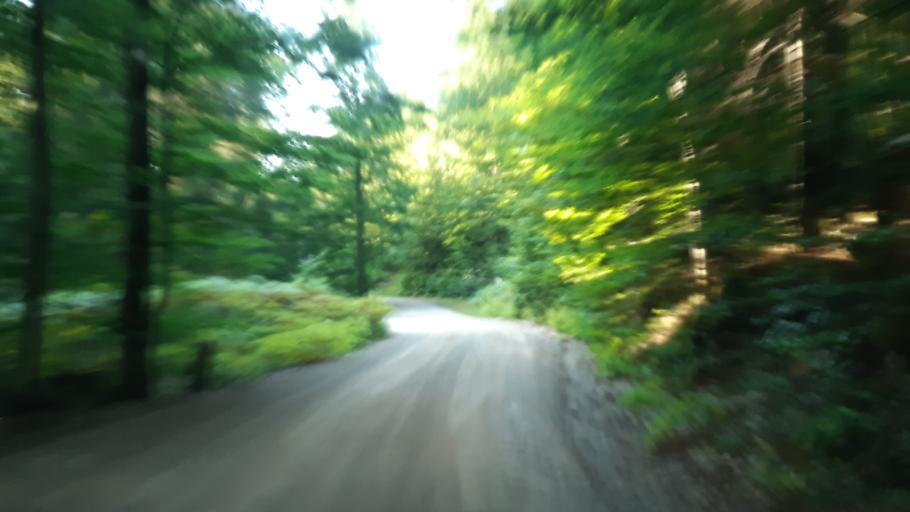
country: SI
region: Kocevje
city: Kocevje
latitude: 45.6727
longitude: 14.9723
